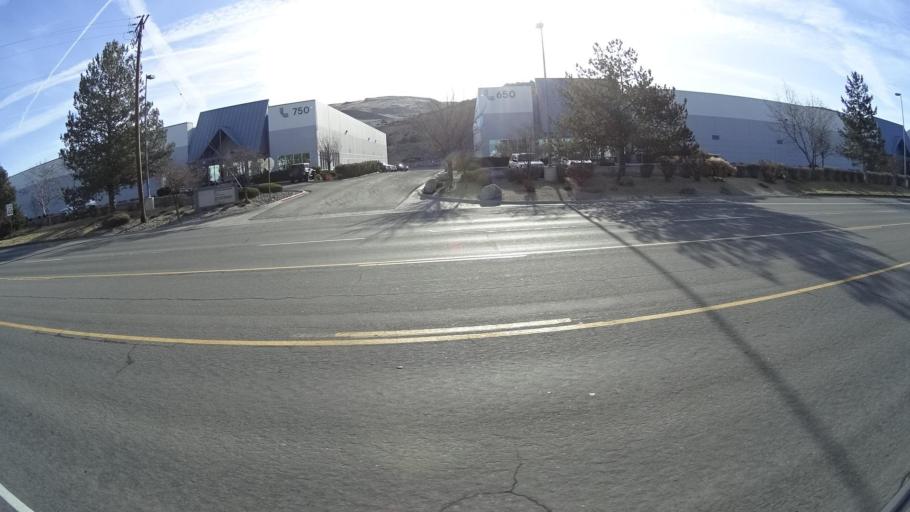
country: US
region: Nevada
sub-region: Washoe County
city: Sparks
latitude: 39.5394
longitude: -119.7033
